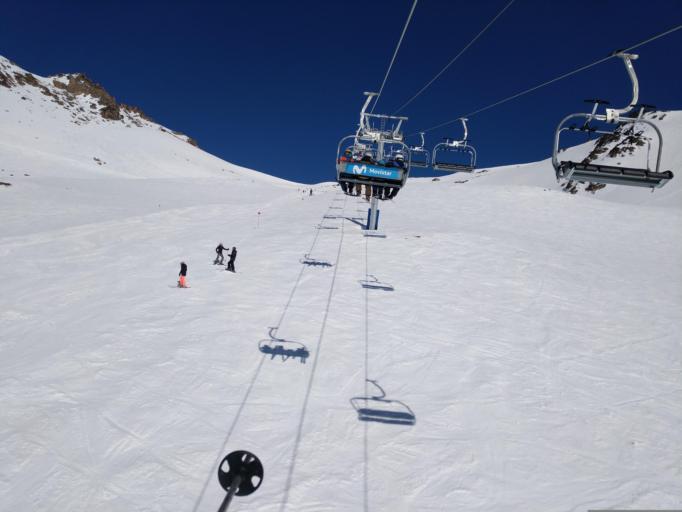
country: AR
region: Rio Negro
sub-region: Departamento de Bariloche
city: San Carlos de Bariloche
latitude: -41.1708
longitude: -71.4792
